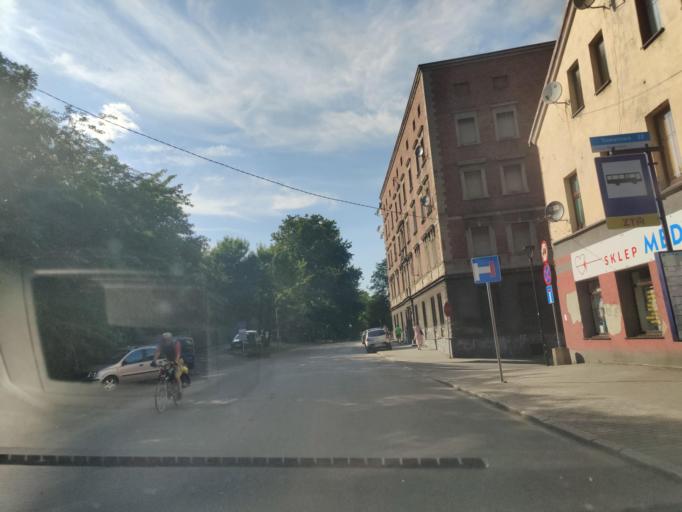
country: PL
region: Silesian Voivodeship
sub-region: Myslowice
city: Myslowice
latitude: 50.2435
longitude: 19.1367
